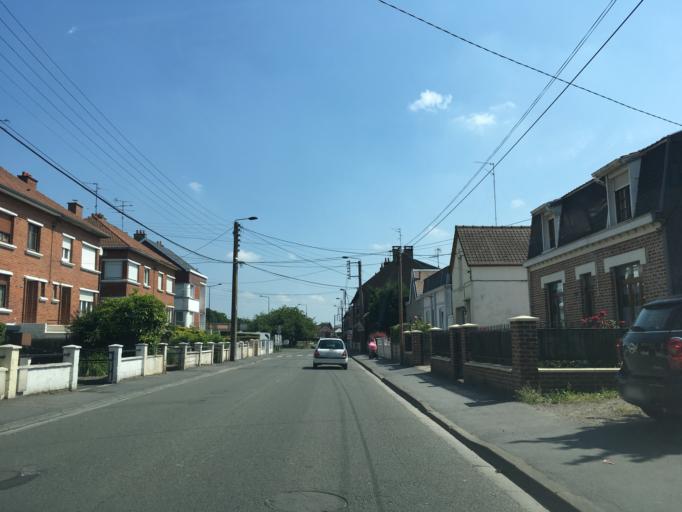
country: FR
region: Nord-Pas-de-Calais
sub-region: Departement du Nord
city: La Sentinelle
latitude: 50.3550
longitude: 3.4923
